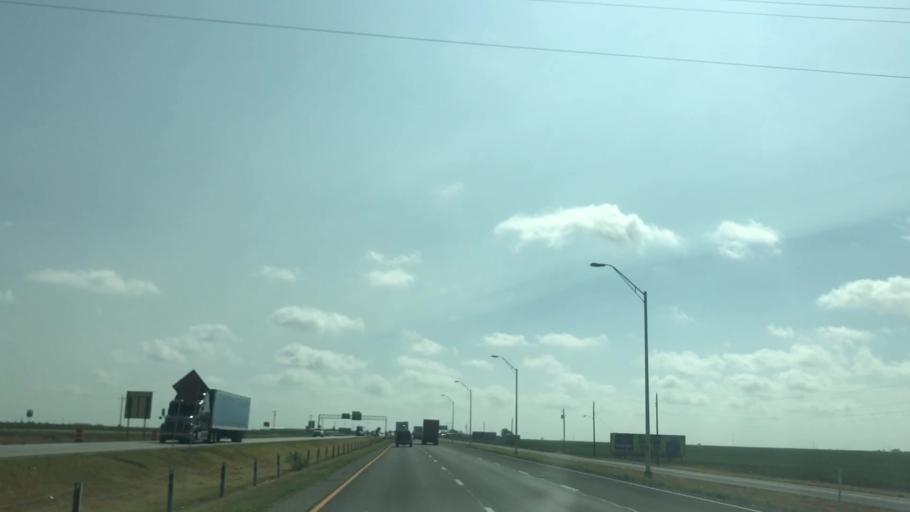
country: US
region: Texas
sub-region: Nolan County
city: Roscoe
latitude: 32.4477
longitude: -100.4975
